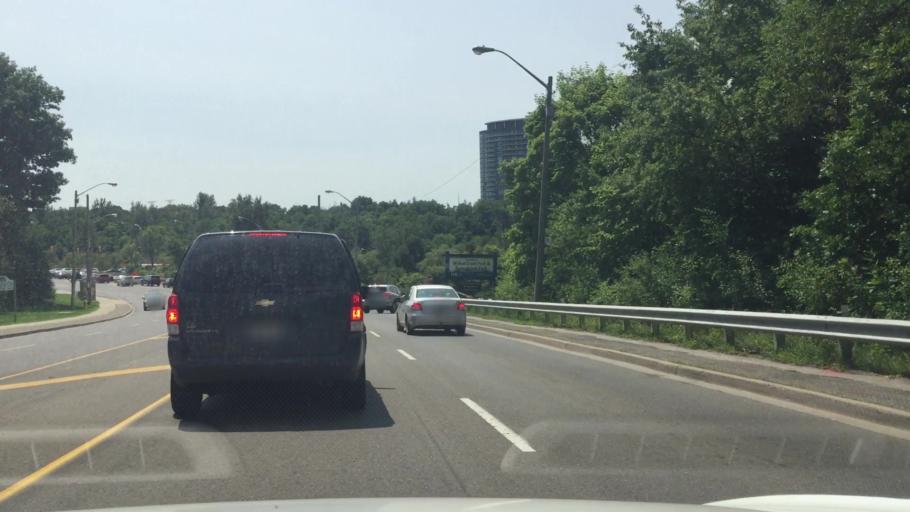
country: CA
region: Ontario
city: Willowdale
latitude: 43.7193
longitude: -79.3503
